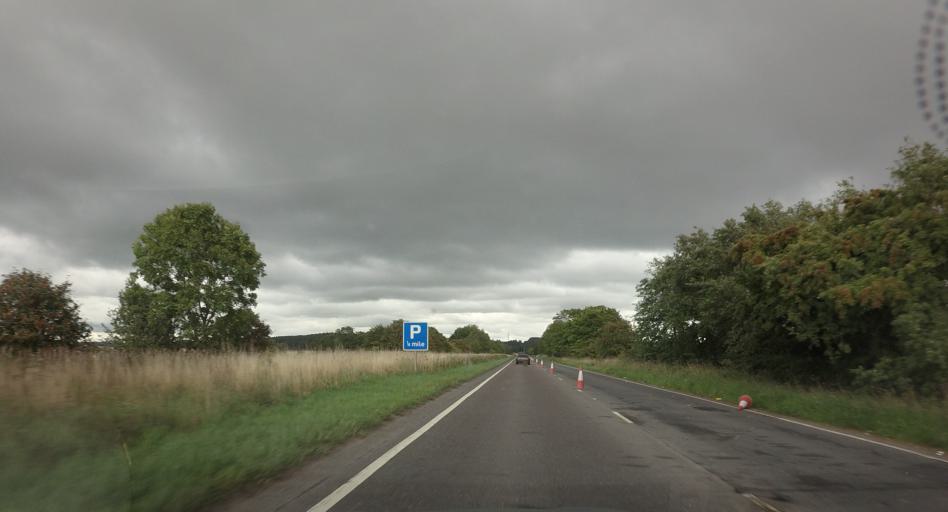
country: GB
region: Scotland
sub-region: Clackmannanshire
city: Clackmannan
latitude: 56.1046
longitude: -3.7332
